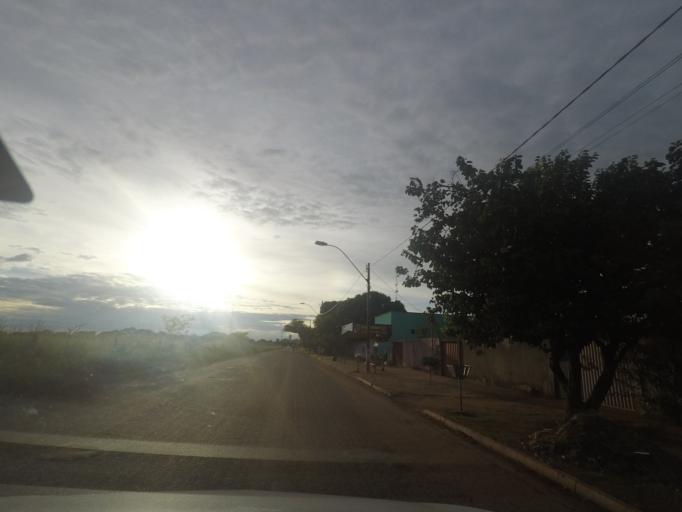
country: BR
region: Goias
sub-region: Trindade
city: Trindade
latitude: -16.7193
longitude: -49.4395
